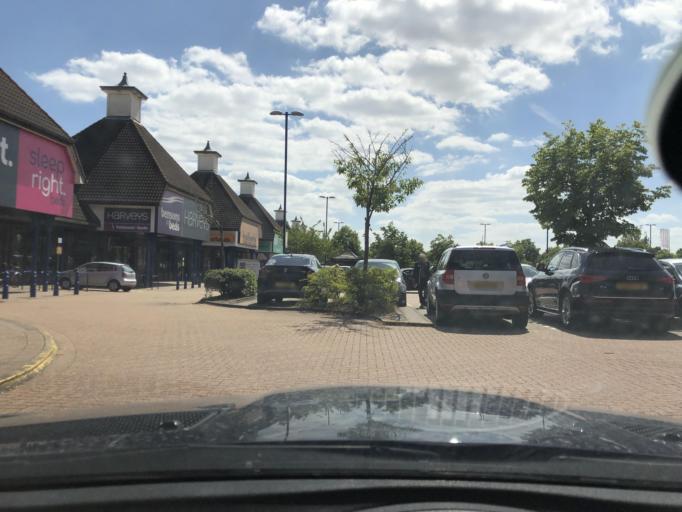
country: GB
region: England
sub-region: Essex
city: Chelmsford
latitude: 51.7340
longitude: 0.4962
